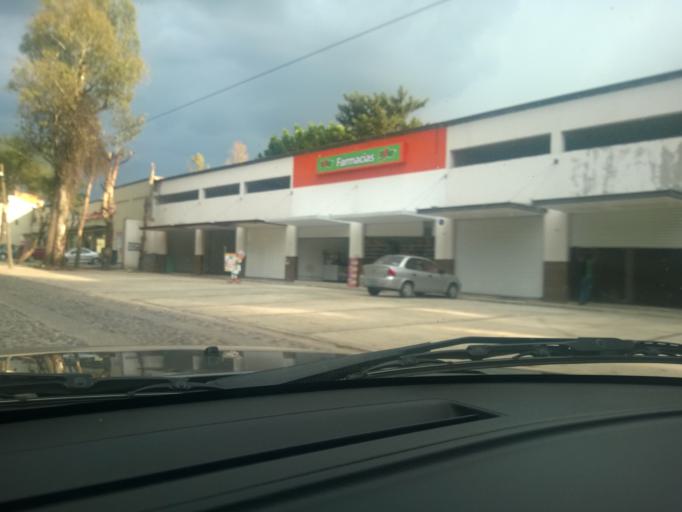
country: MX
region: Guanajuato
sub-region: Leon
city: Fraccionamiento Paraiso Real
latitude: 21.1129
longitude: -101.6163
